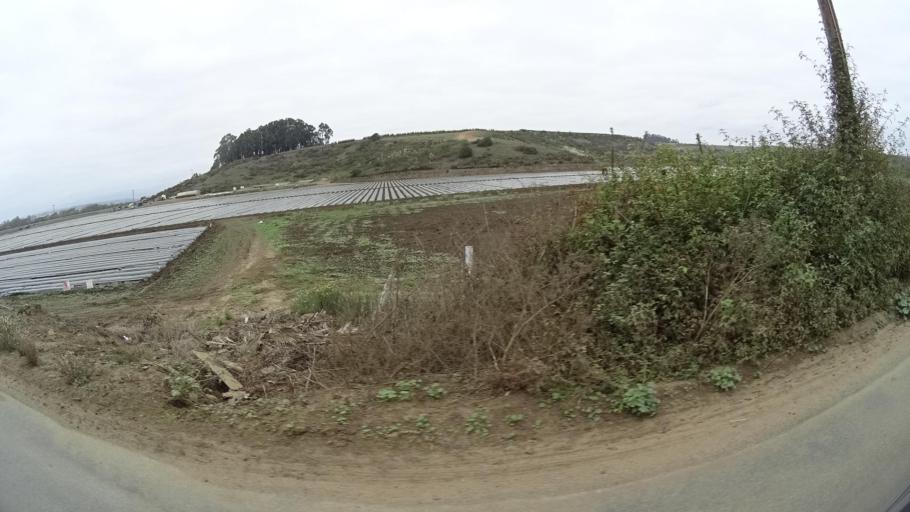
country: US
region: California
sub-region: Monterey County
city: Las Lomas
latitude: 36.8613
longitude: -121.7965
